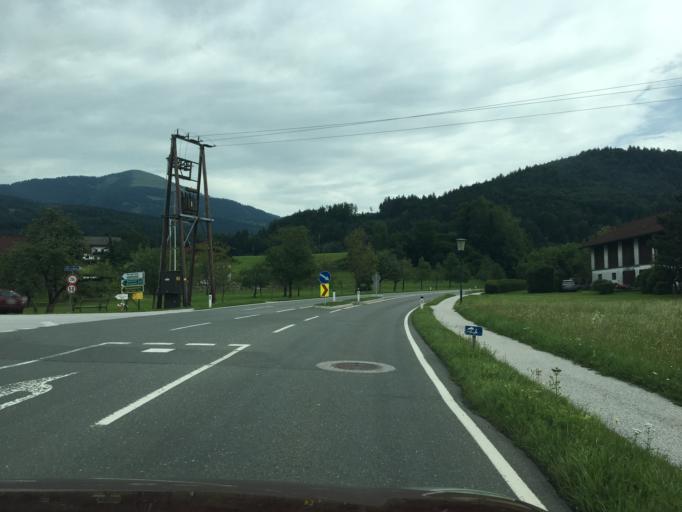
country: AT
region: Salzburg
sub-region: Politischer Bezirk Hallein
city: Adnet
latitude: 47.6625
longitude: 13.1495
